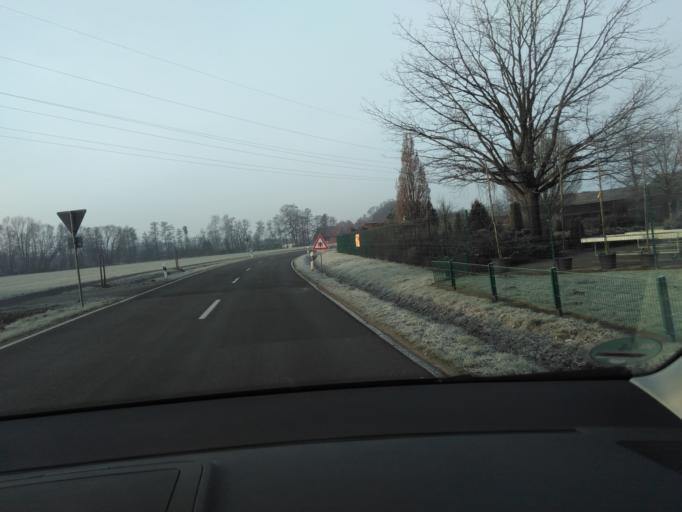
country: DE
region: North Rhine-Westphalia
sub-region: Regierungsbezirk Detmold
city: Verl
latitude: 51.8637
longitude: 8.4964
